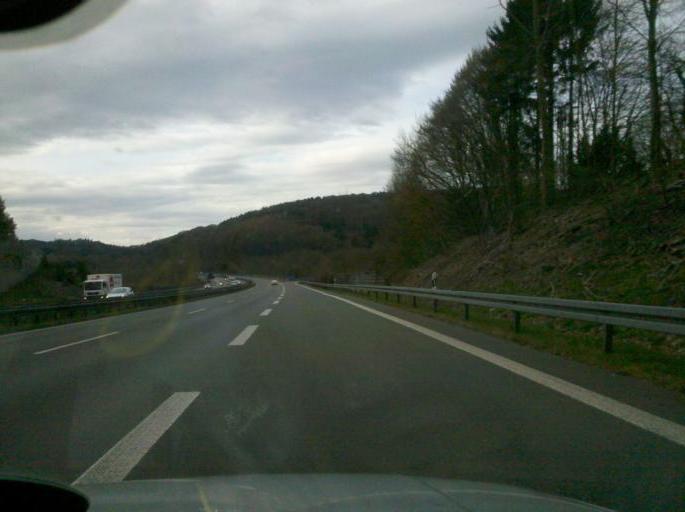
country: DE
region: North Rhine-Westphalia
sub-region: Regierungsbezirk Koln
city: Overath
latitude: 50.9463
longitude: 7.2223
